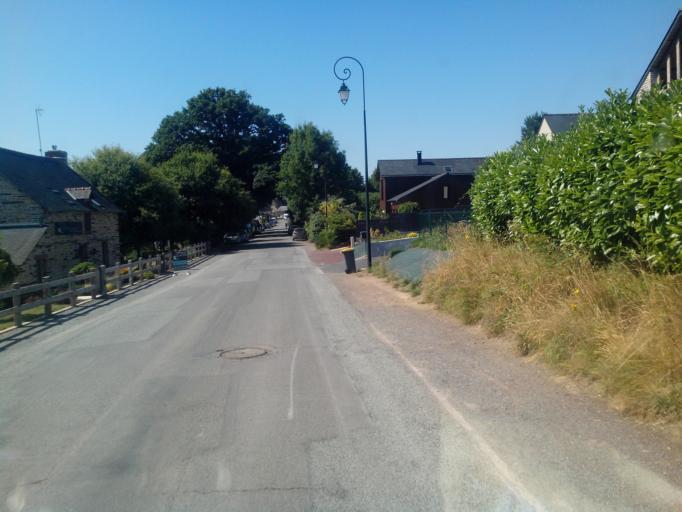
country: FR
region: Brittany
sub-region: Departement d'Ille-et-Vilaine
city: Paimpont
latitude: 48.0159
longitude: -2.1718
